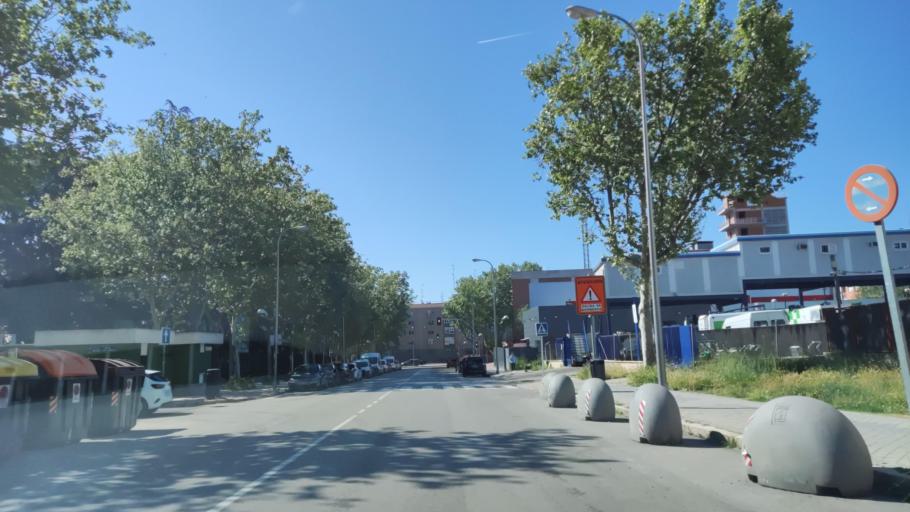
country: ES
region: Madrid
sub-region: Provincia de Madrid
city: San Blas
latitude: 40.4294
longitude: -3.6156
